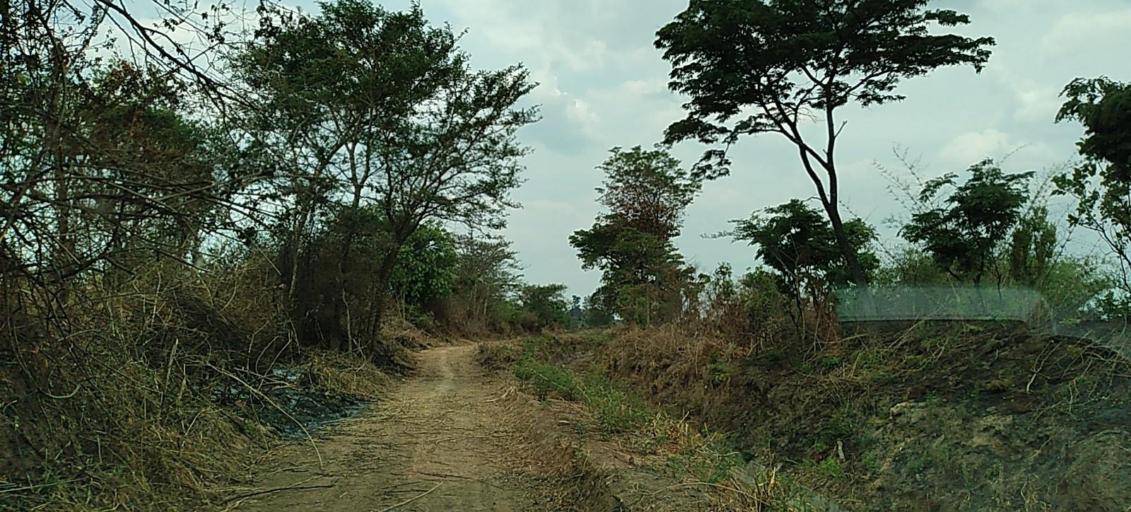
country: ZM
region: Copperbelt
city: Chililabombwe
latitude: -12.3595
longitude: 27.8028
